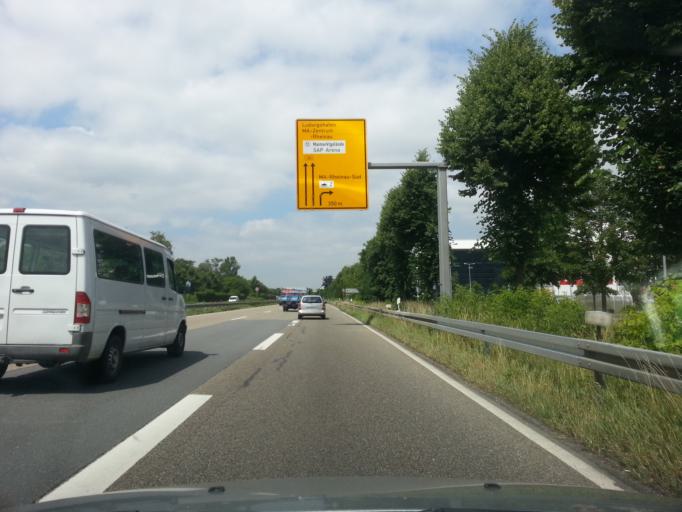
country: DE
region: Baden-Wuerttemberg
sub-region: Karlsruhe Region
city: Bruhl
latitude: 49.4135
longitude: 8.5429
